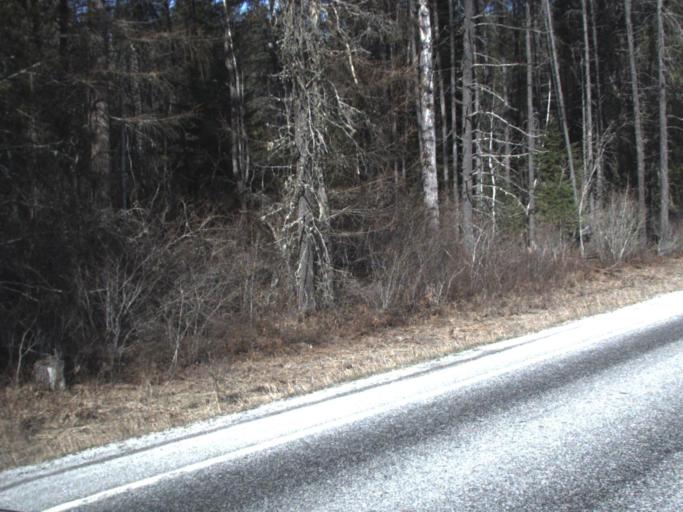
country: CA
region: British Columbia
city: Fruitvale
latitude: 48.6533
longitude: -117.3841
